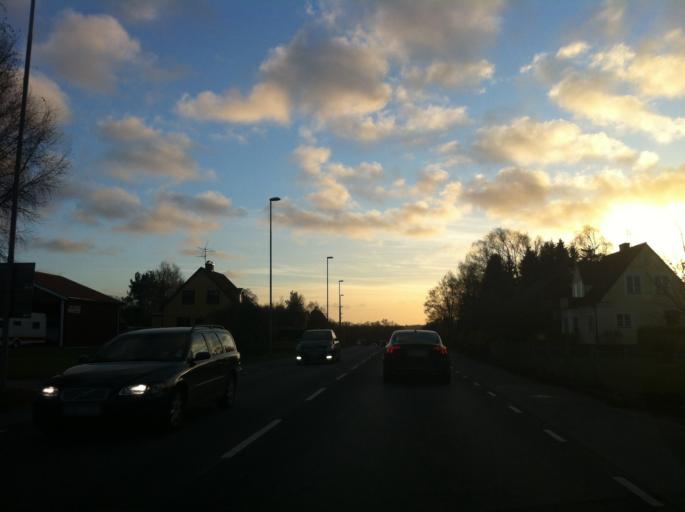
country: SE
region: Skane
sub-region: Hoors Kommun
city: Hoeoer
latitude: 55.9466
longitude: 13.5602
